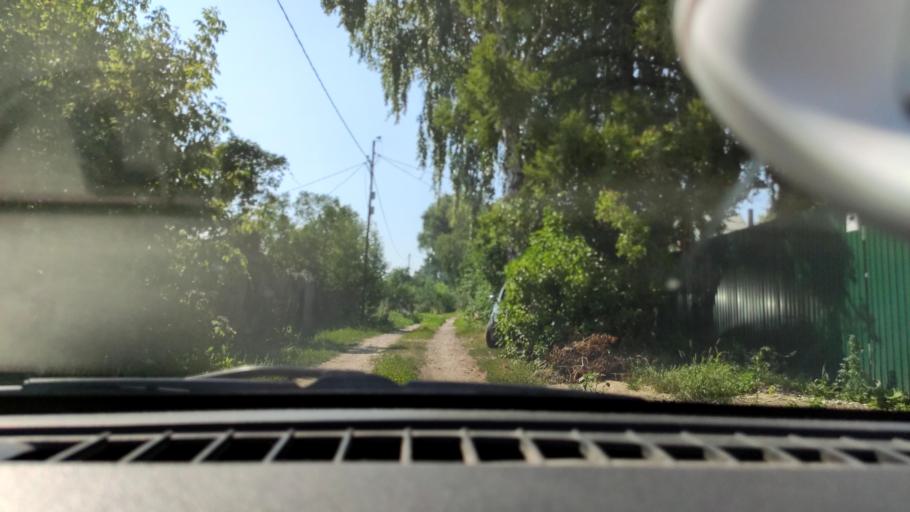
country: RU
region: Samara
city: Petra-Dubrava
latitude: 53.2685
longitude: 50.2989
